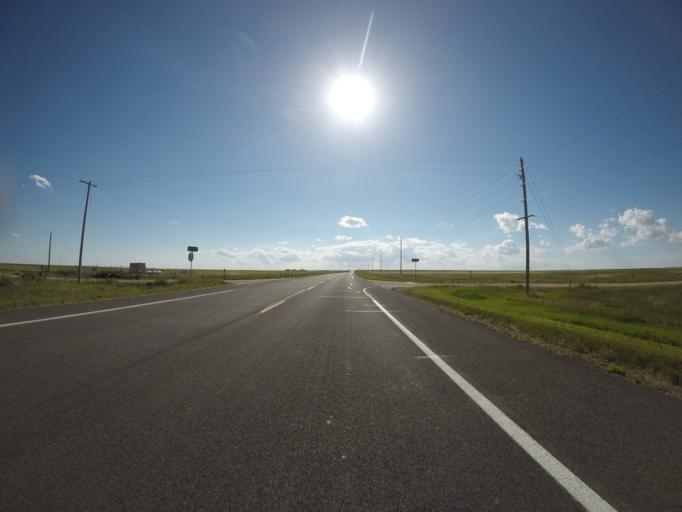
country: US
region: Colorado
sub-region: Morgan County
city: Brush
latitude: 40.6097
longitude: -103.6955
